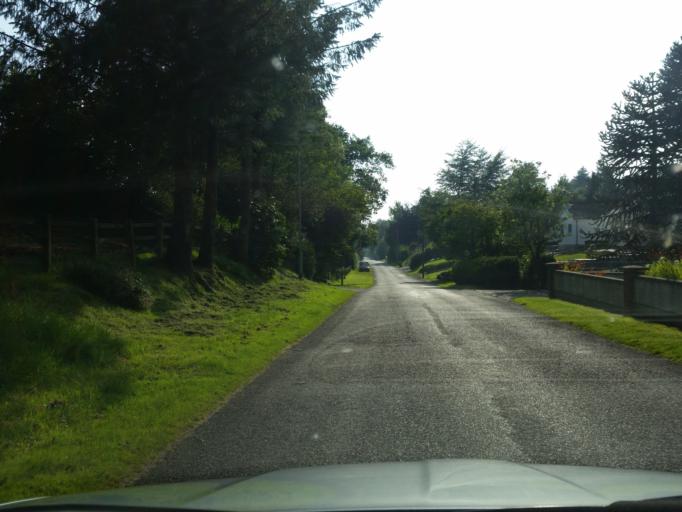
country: GB
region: Northern Ireland
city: Ballinamallard
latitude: 54.3225
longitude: -7.5275
